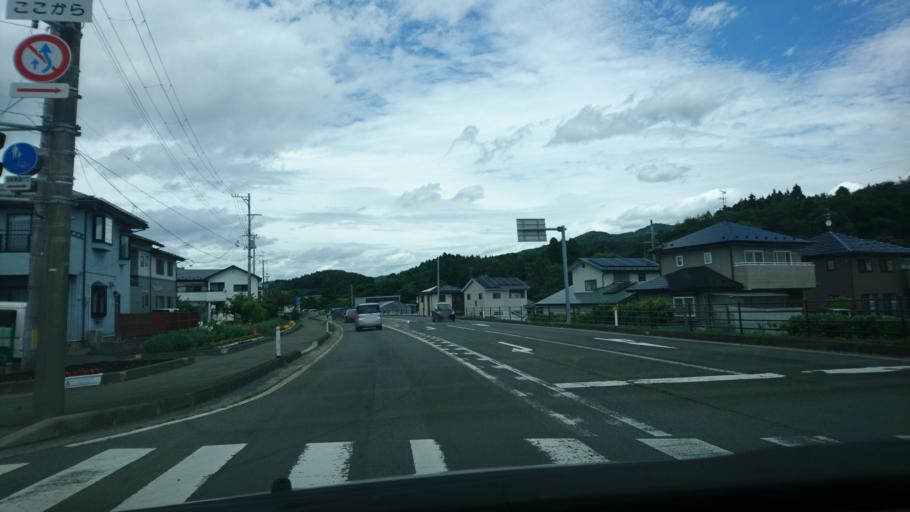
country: JP
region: Iwate
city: Morioka-shi
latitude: 39.6073
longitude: 141.2037
